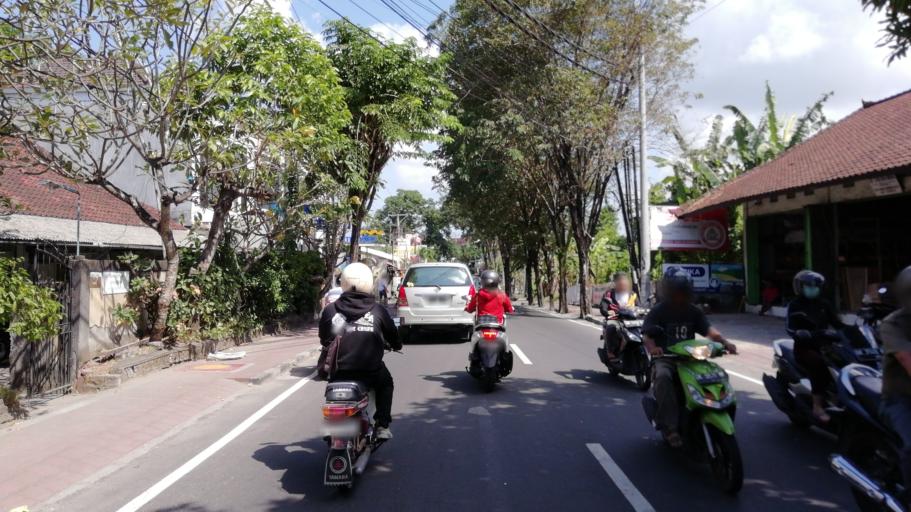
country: ID
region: Bali
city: Banjar Gunungpande
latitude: -8.6465
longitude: 115.1664
